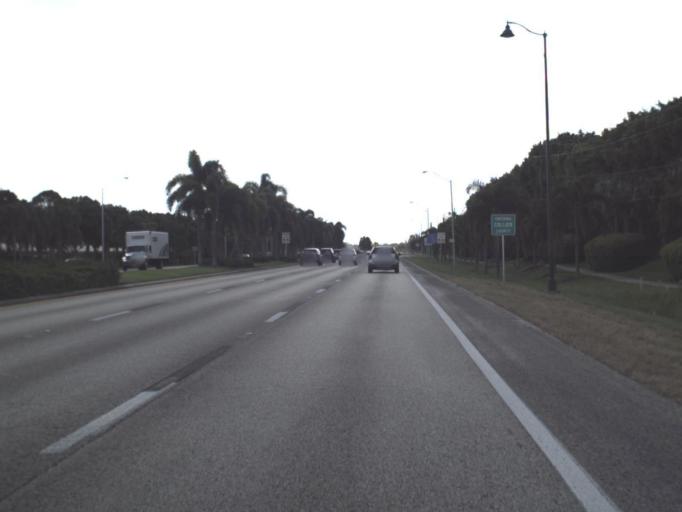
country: US
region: Florida
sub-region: Lee County
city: Bonita Springs
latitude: 26.3169
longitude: -81.8052
